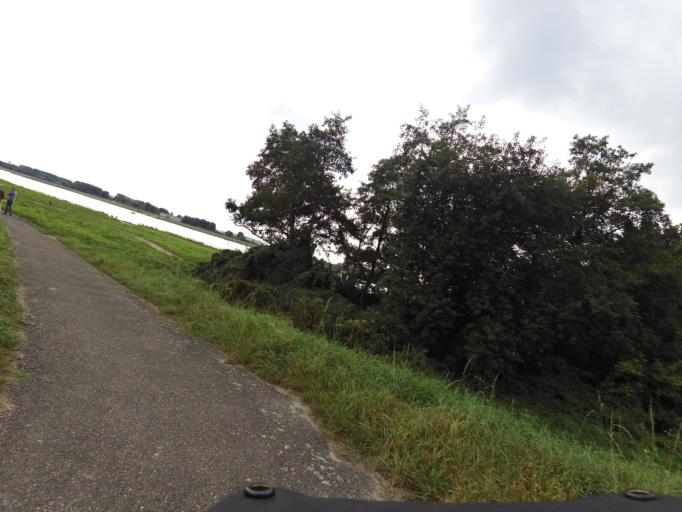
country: NL
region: South Holland
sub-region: Gemeente Maassluis
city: Maassluis
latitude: 51.9316
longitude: 4.2260
